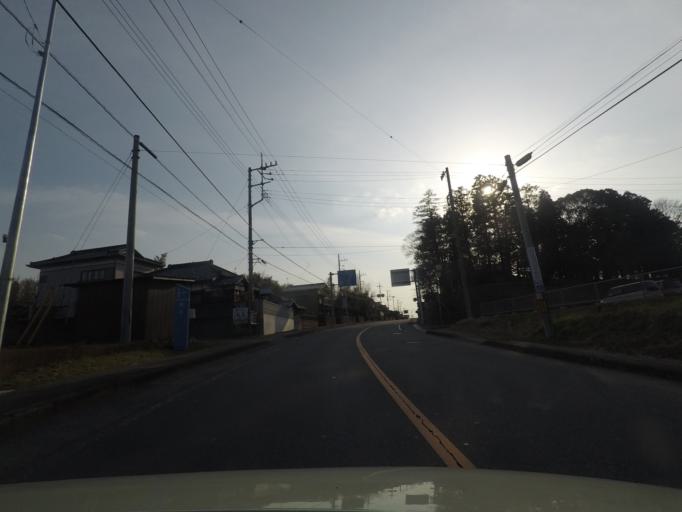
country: JP
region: Ibaraki
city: Okunoya
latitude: 36.2847
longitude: 140.4209
